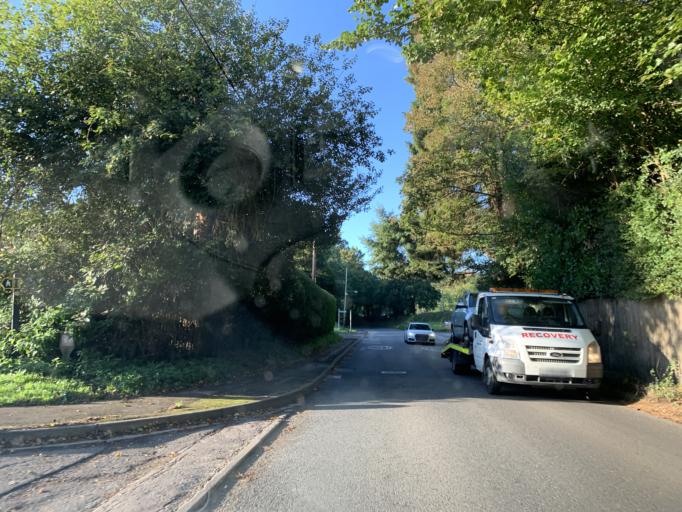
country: GB
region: England
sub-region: Wiltshire
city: Whiteparish
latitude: 50.9760
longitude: -1.6377
